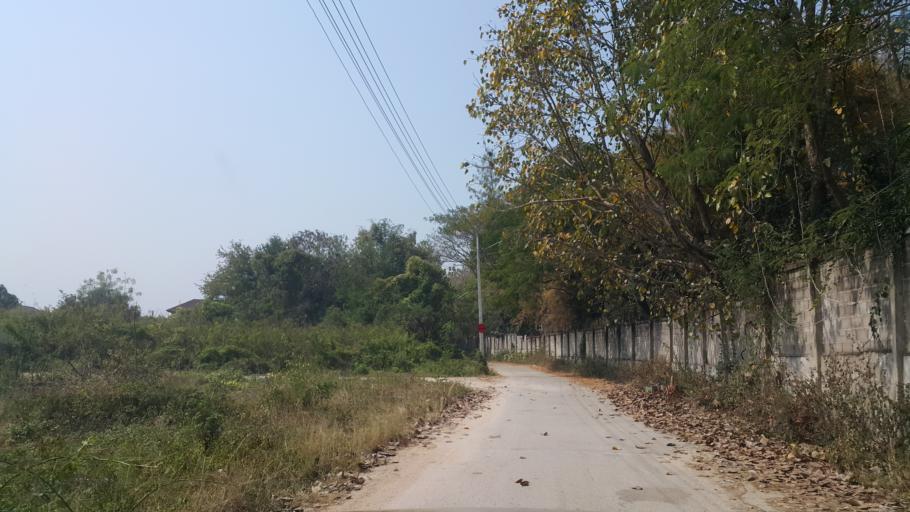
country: TH
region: Lampang
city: Lampang
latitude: 18.2842
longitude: 99.4470
